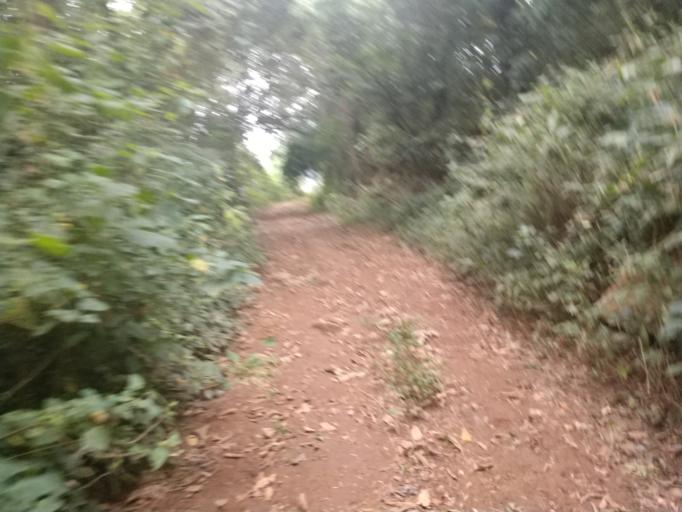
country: MX
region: Nayarit
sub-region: Tepic
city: La Corregidora
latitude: 21.4690
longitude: -104.7877
